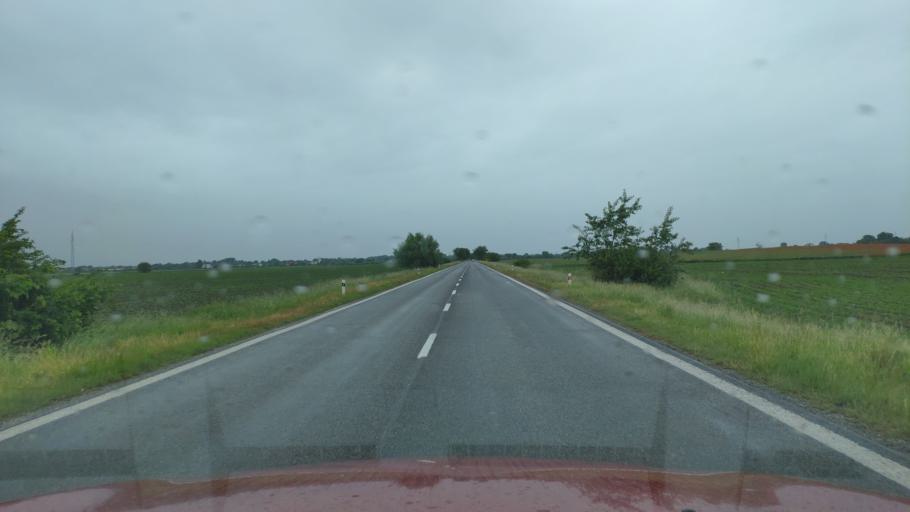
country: HU
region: Borsod-Abauj-Zemplen
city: Karcsa
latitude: 48.4188
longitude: 21.8333
